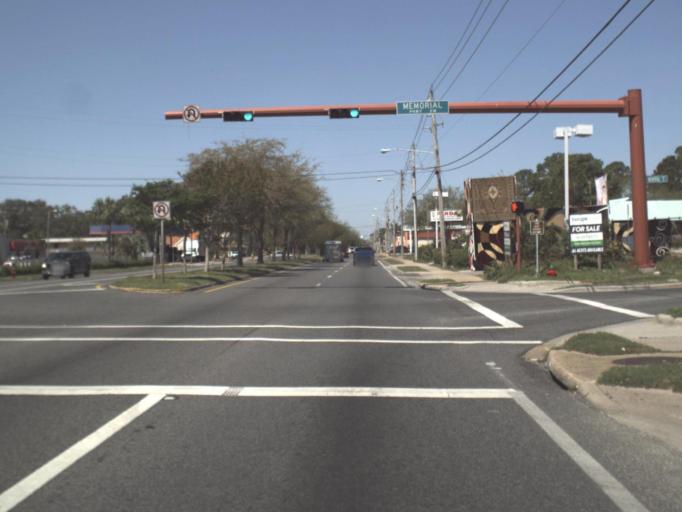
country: US
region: Florida
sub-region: Okaloosa County
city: Fort Walton Beach
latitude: 30.4063
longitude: -86.6307
